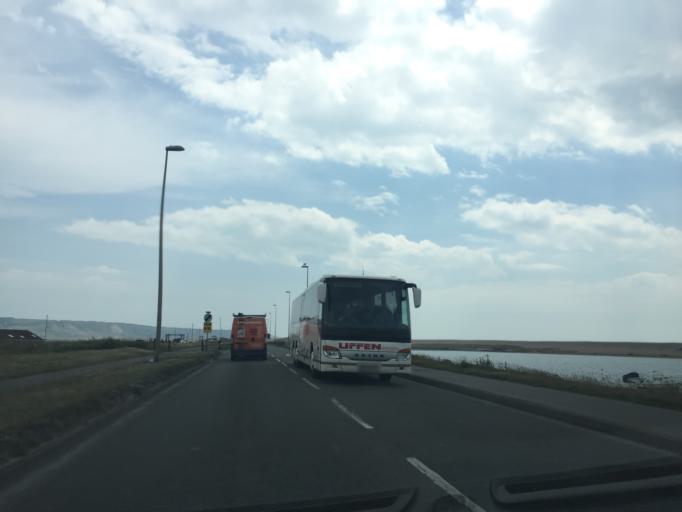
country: GB
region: England
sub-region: Dorset
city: Weymouth
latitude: 50.5847
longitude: -2.4718
